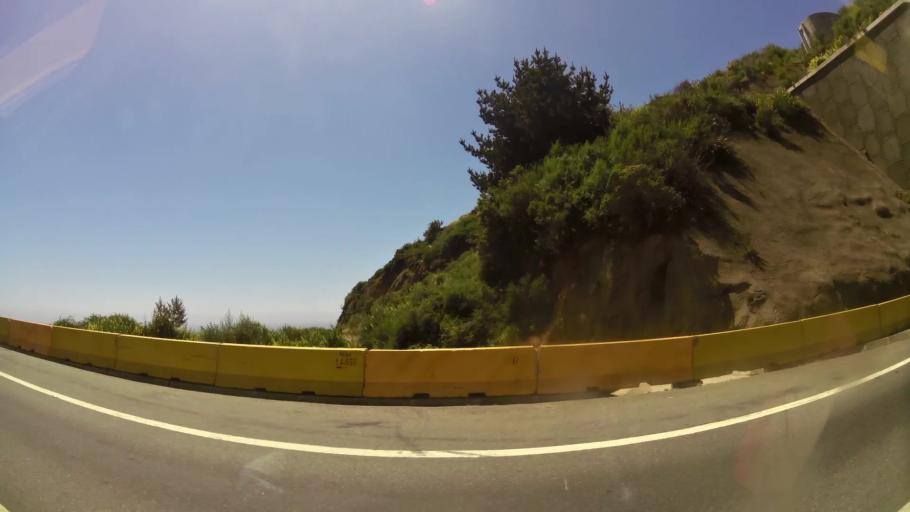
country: CL
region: Valparaiso
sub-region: Provincia de Valparaiso
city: Valparaiso
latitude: -33.0461
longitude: -71.6549
